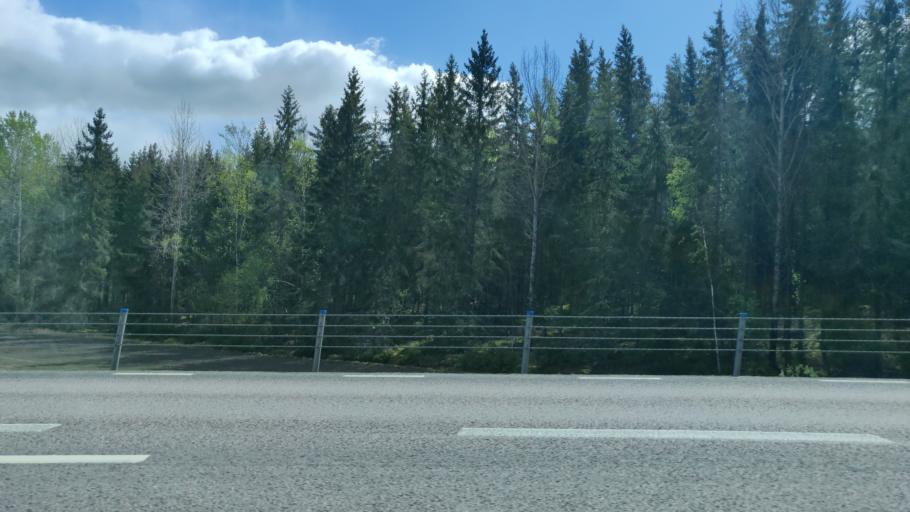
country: SE
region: Vaermland
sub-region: Karlstads Kommun
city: Skattkarr
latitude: 59.4950
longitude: 13.6061
